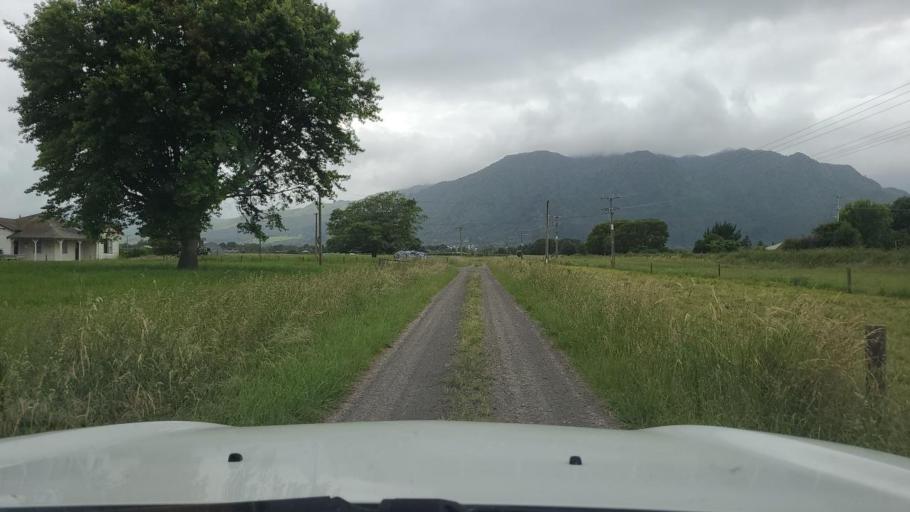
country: NZ
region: Waikato
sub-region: Hauraki District
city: Paeroa
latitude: -37.5603
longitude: 175.6849
